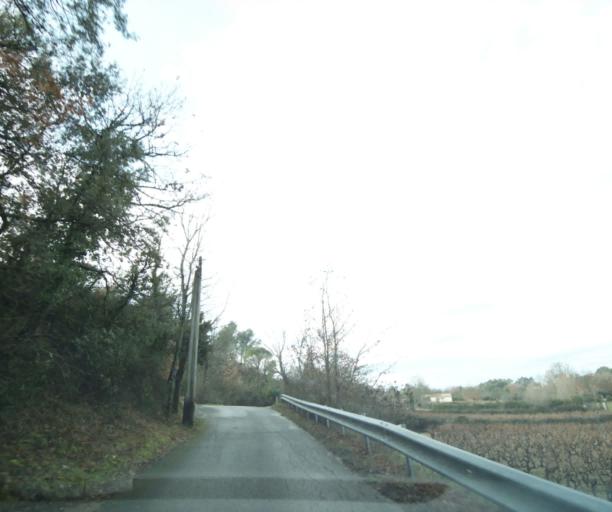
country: FR
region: Provence-Alpes-Cote d'Azur
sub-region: Departement du Var
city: Tourves
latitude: 43.4033
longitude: 5.9086
